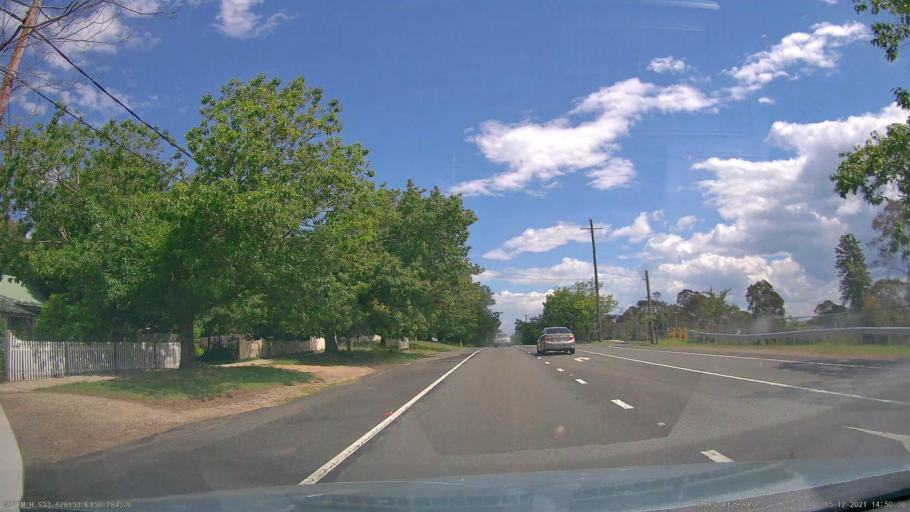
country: AU
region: New South Wales
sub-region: Blue Mountains Municipality
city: Blackheath
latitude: -33.6284
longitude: 150.2846
